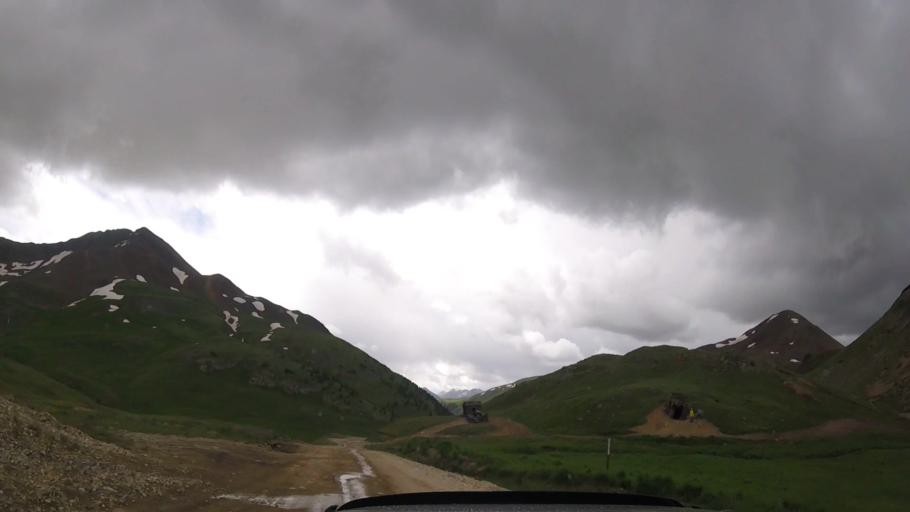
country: US
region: Colorado
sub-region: Ouray County
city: Ouray
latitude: 37.9527
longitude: -107.5746
